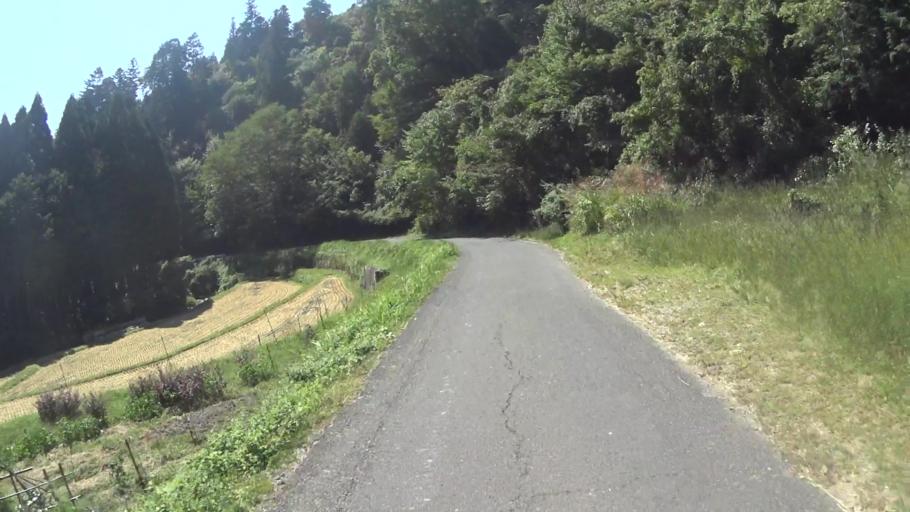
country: JP
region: Kyoto
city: Kameoka
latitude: 34.9396
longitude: 135.5679
